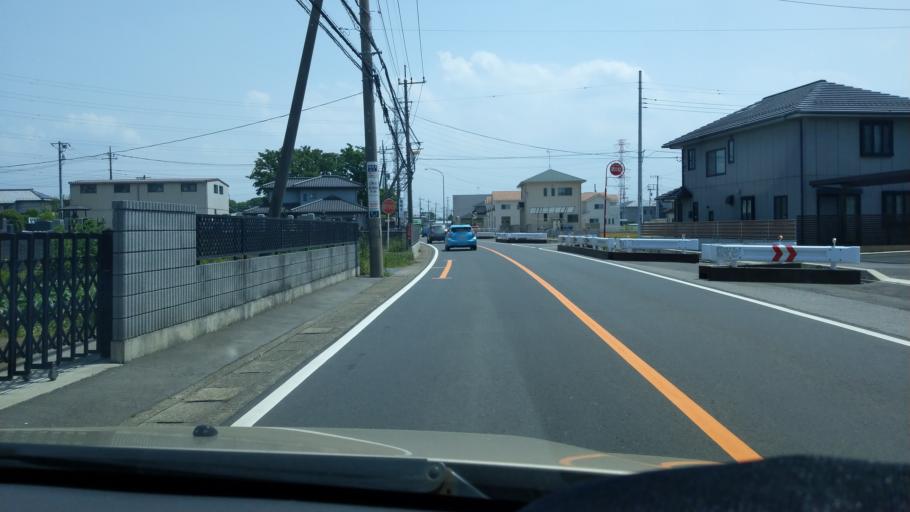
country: JP
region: Saitama
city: Koshigaya
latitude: 35.9041
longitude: 139.7328
